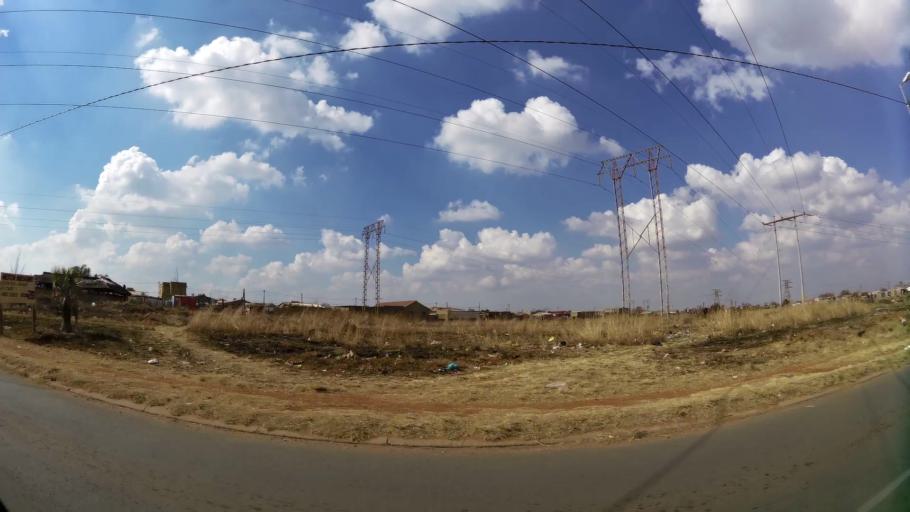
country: ZA
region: Gauteng
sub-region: City of Johannesburg Metropolitan Municipality
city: Roodepoort
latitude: -26.1888
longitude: 27.8562
